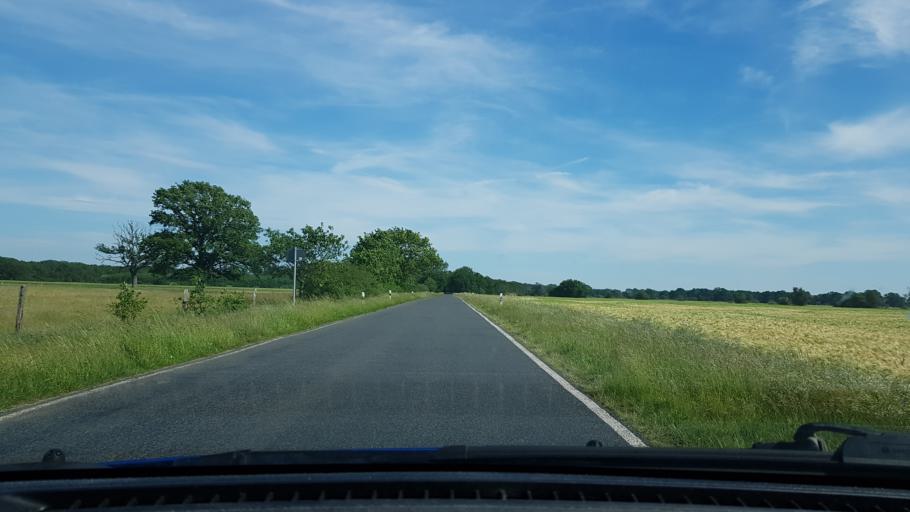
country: DE
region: Lower Saxony
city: Neu Darchau
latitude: 53.3358
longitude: 10.8635
